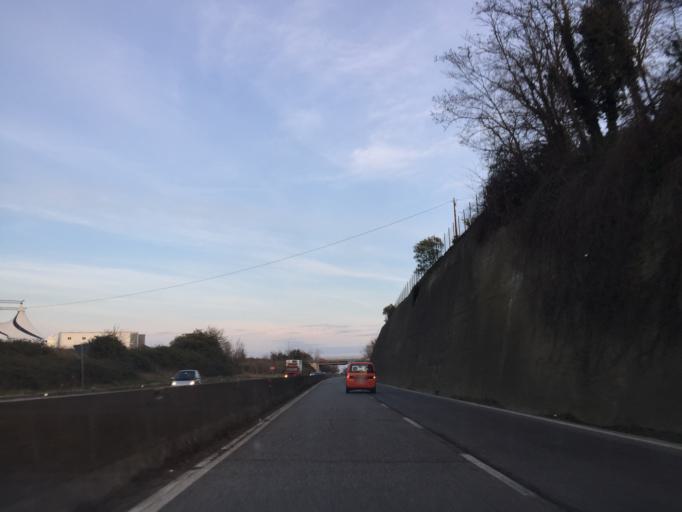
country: IT
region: Latium
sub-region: Citta metropolitana di Roma Capitale
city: Formello
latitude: 42.0464
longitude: 12.3914
